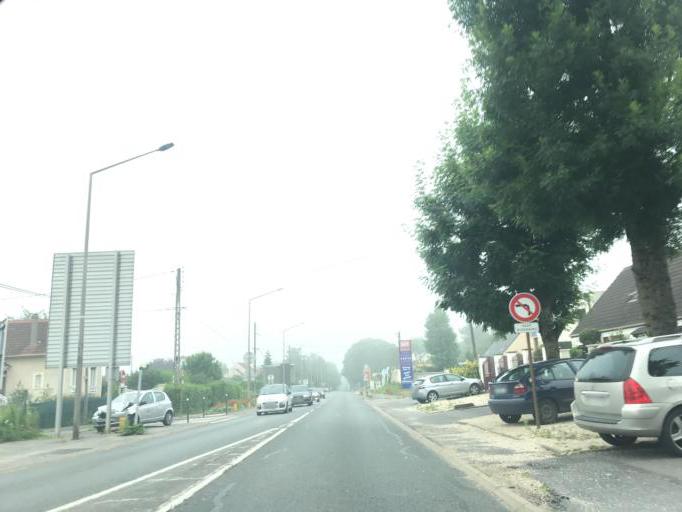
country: FR
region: Ile-de-France
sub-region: Departement de Seine-et-Marne
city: Thorigny-sur-Marne
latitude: 48.8776
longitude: 2.7276
